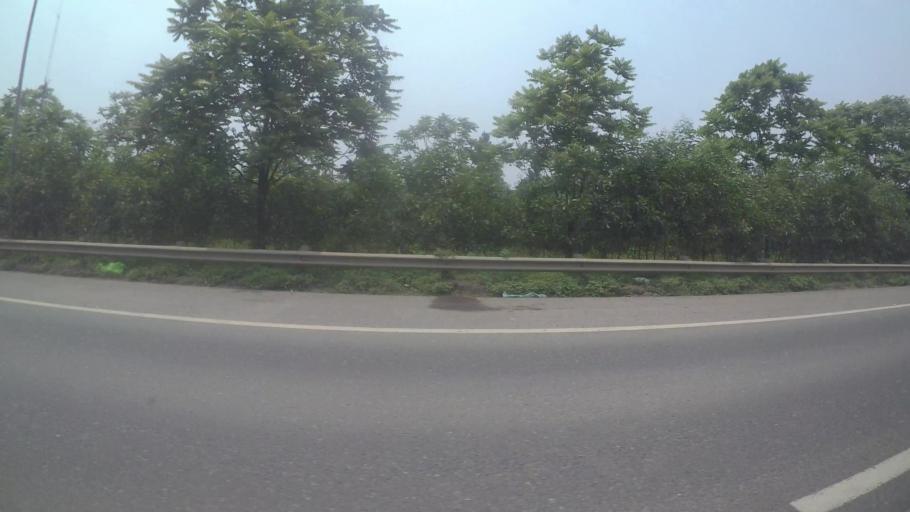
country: VN
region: Ha Noi
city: Lien Quan
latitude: 20.9902
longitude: 105.5522
